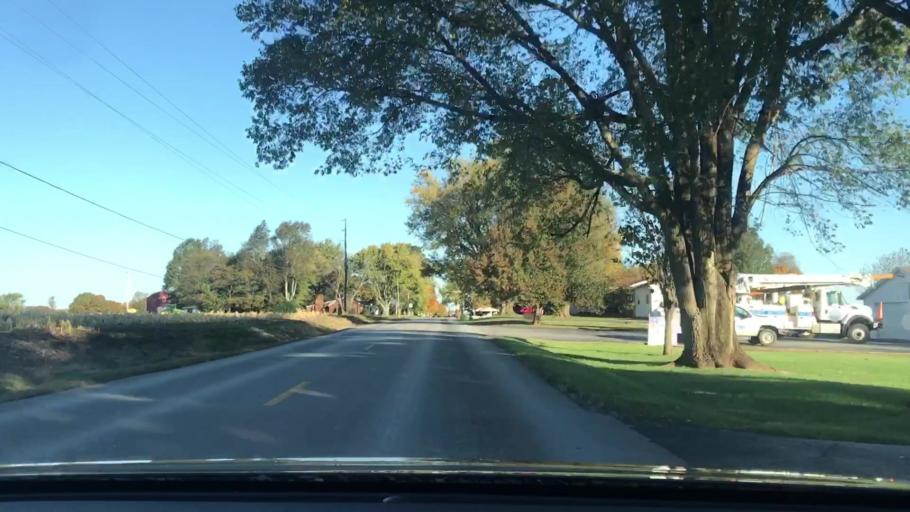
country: US
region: Kentucky
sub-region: Logan County
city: Auburn
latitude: 36.8537
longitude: -86.7077
